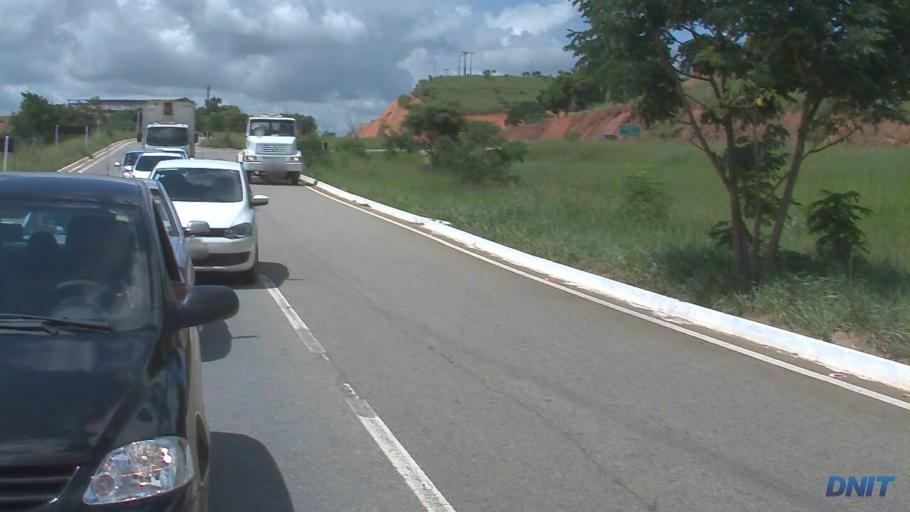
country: BR
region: Minas Gerais
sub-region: Governador Valadares
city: Governador Valadares
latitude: -18.9075
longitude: -42.0047
